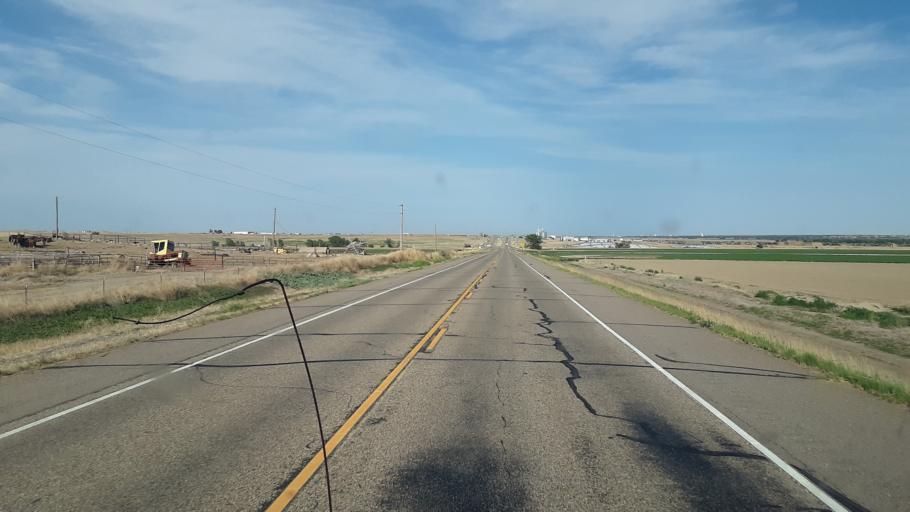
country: US
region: Colorado
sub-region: Prowers County
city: Lamar
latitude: 38.1142
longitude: -102.7482
